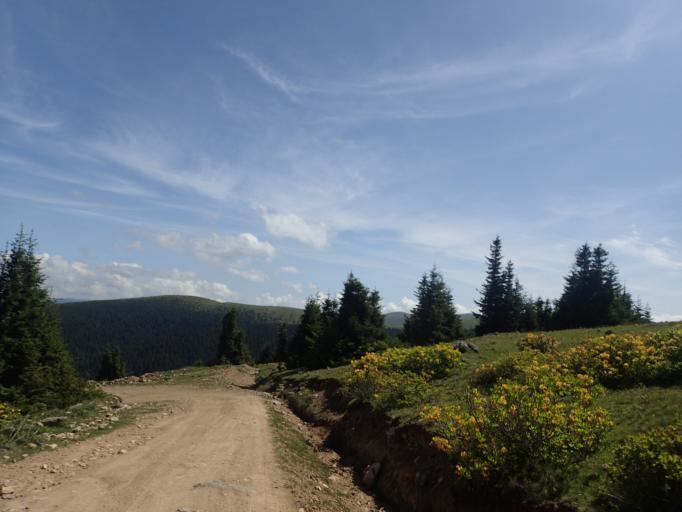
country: TR
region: Ordu
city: Topcam
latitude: 40.6371
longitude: 37.9532
